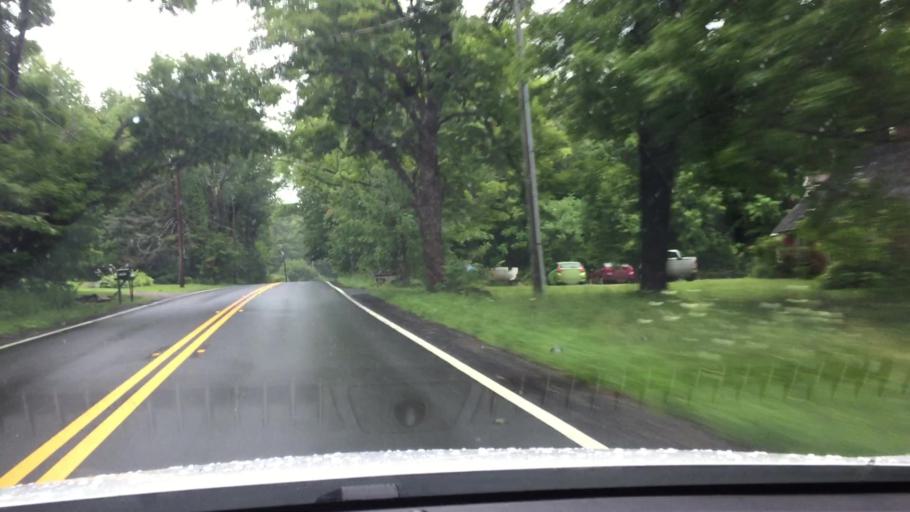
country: US
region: Massachusetts
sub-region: Berkshire County
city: Becket
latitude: 42.3416
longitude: -73.1138
